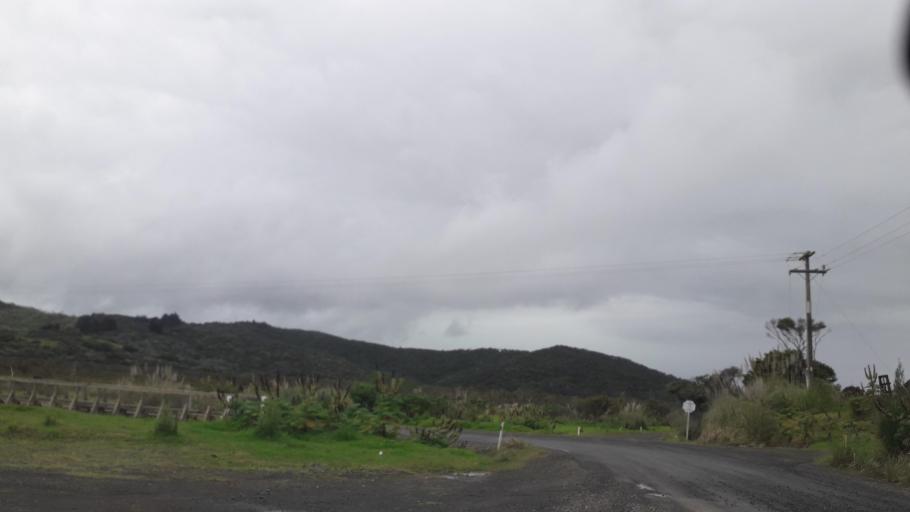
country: NZ
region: Northland
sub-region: Far North District
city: Kaitaia
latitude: -35.4084
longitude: 173.3824
